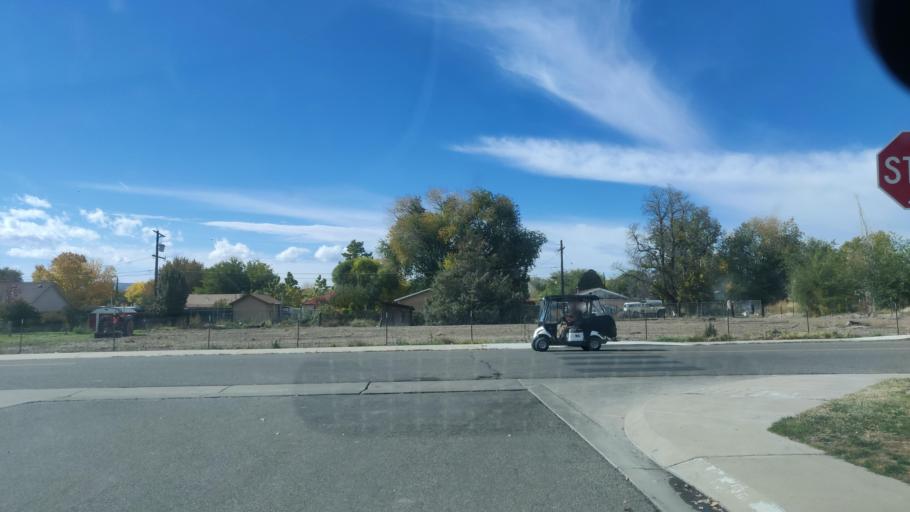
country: US
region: Colorado
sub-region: Mesa County
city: Fruitvale
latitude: 39.0806
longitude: -108.5103
